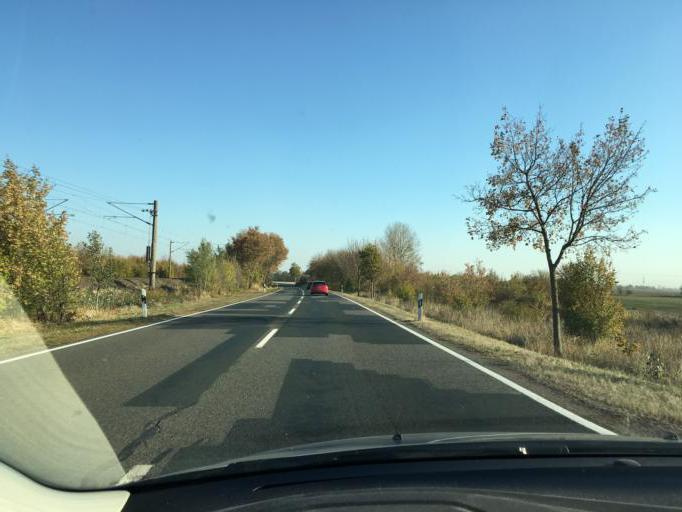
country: DE
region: Saxony-Anhalt
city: Roitzsch
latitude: 51.5606
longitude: 12.2938
